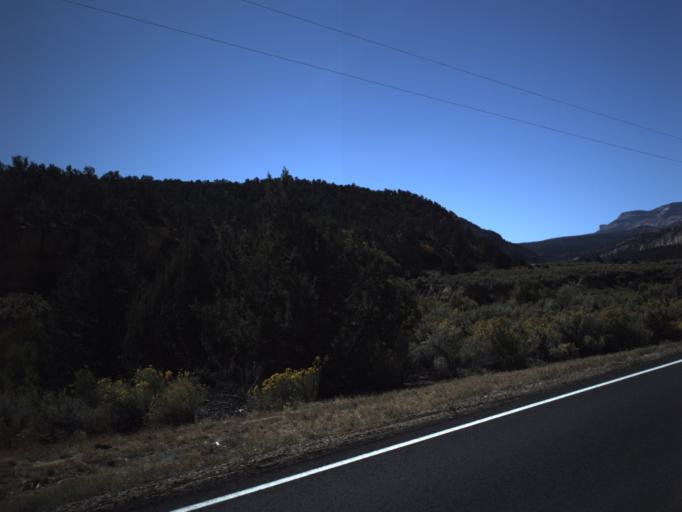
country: US
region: Utah
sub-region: Wayne County
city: Loa
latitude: 37.7382
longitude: -111.7365
